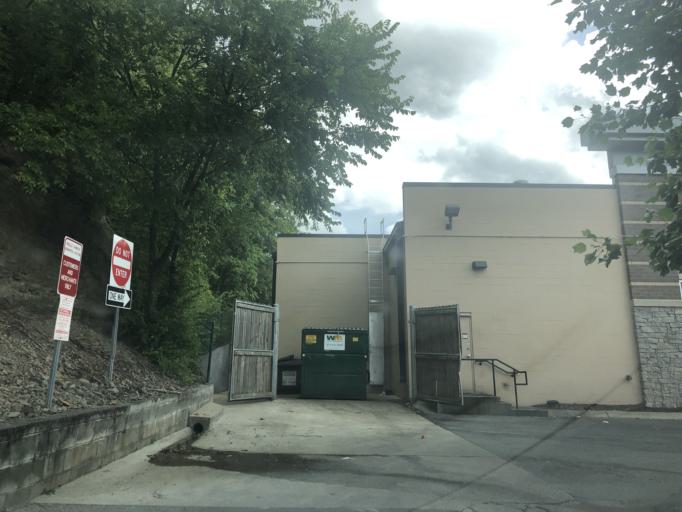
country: US
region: Tennessee
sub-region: Davidson County
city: Belle Meade
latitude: 36.0760
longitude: -86.9195
